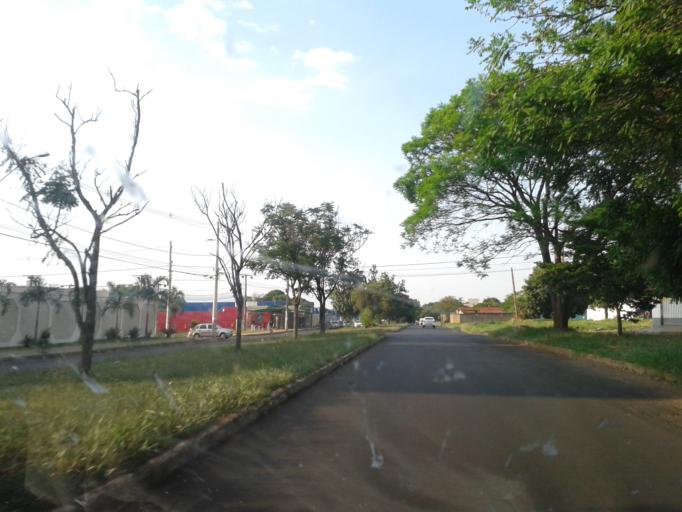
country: BR
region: Minas Gerais
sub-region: Uberlandia
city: Uberlandia
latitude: -18.9347
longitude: -48.3206
